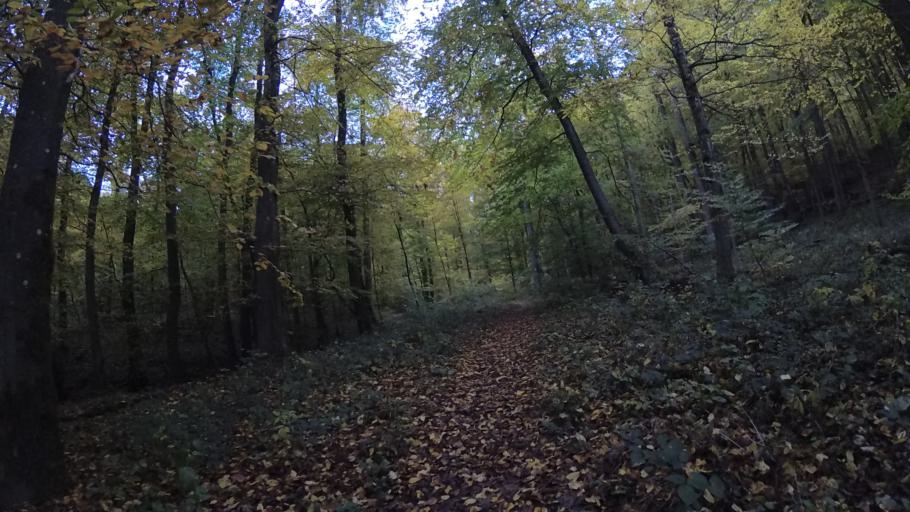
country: DE
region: Saarland
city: Sankt Wendel
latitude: 49.4556
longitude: 7.2017
